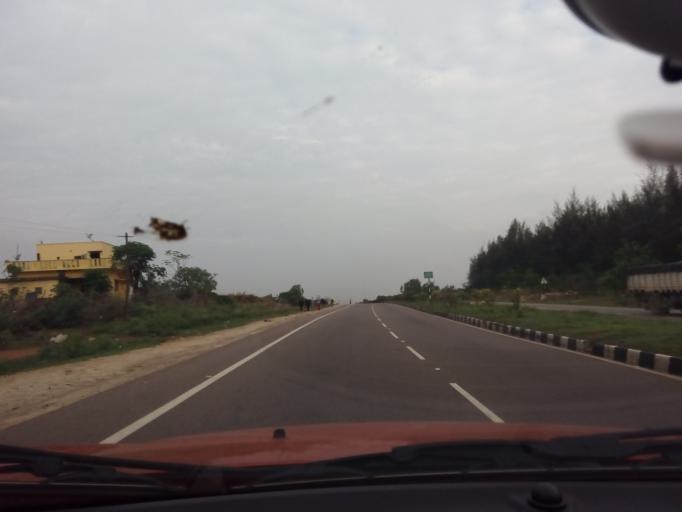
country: IN
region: Karnataka
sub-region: Tumkur
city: Kunigal
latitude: 12.9959
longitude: 76.9313
